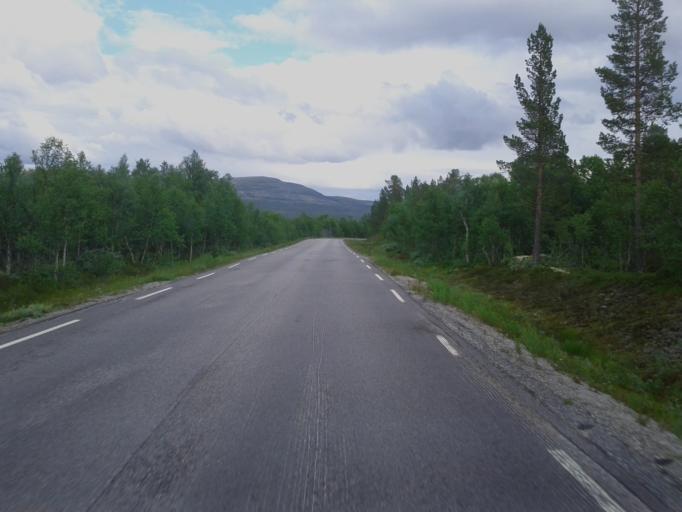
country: NO
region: Sor-Trondelag
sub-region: Roros
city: Roros
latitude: 62.3095
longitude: 11.6813
